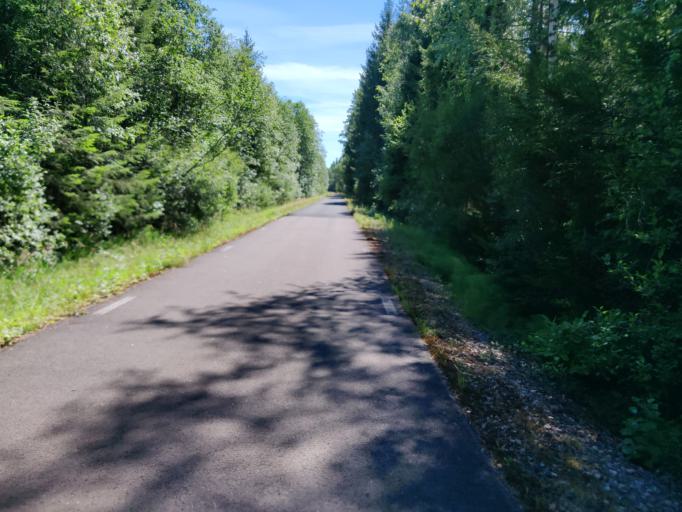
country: SE
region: Vaermland
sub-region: Hagfors Kommun
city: Hagfors
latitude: 59.9715
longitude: 13.5721
